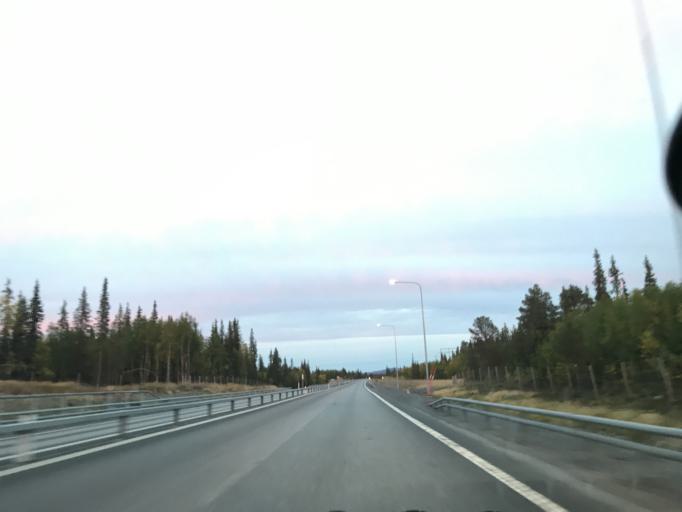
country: SE
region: Norrbotten
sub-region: Gallivare Kommun
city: Malmberget
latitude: 67.6937
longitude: 20.8142
